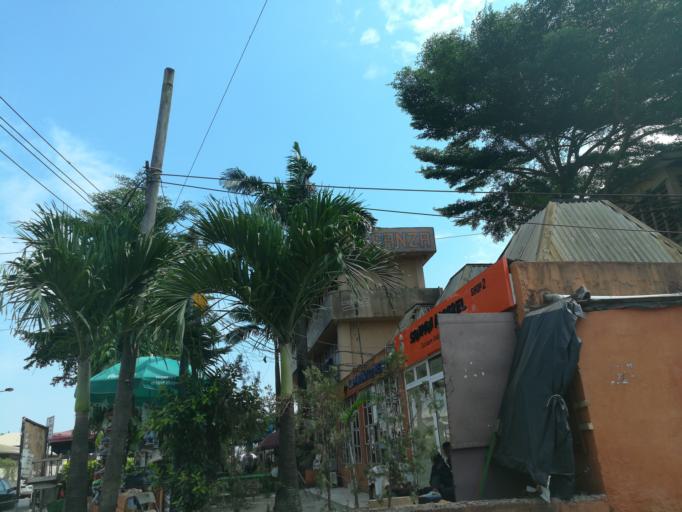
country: NG
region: Lagos
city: Oshodi
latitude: 6.5457
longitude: 3.3264
